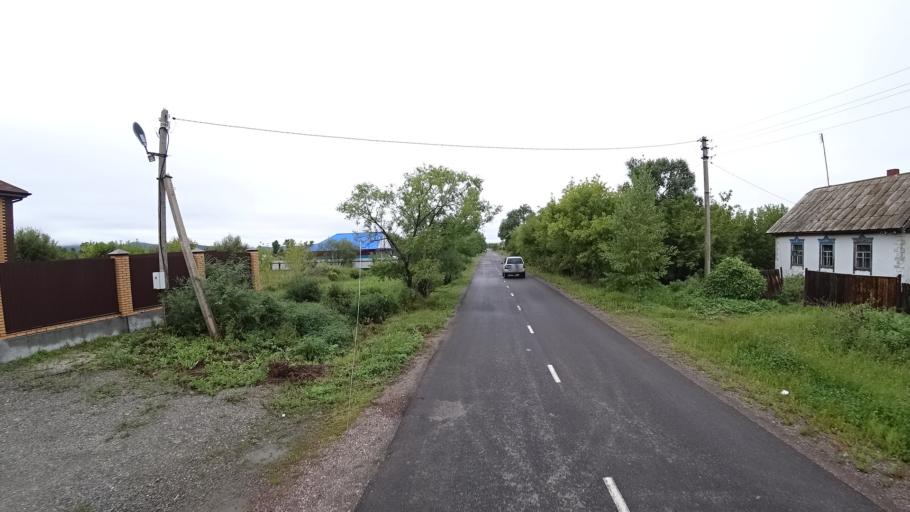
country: RU
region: Primorskiy
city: Monastyrishche
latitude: 44.1989
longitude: 132.4888
